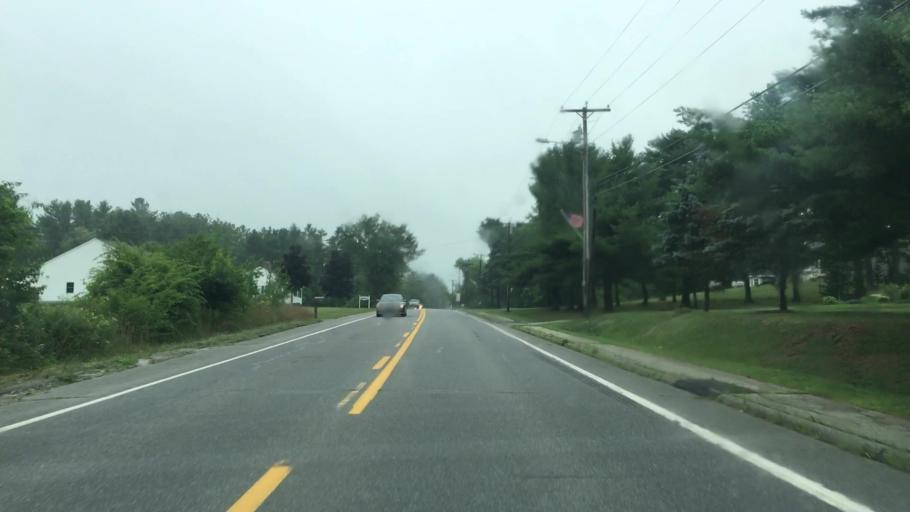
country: US
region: Maine
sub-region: Lincoln County
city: Wiscasset
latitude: 44.0182
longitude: -69.6683
